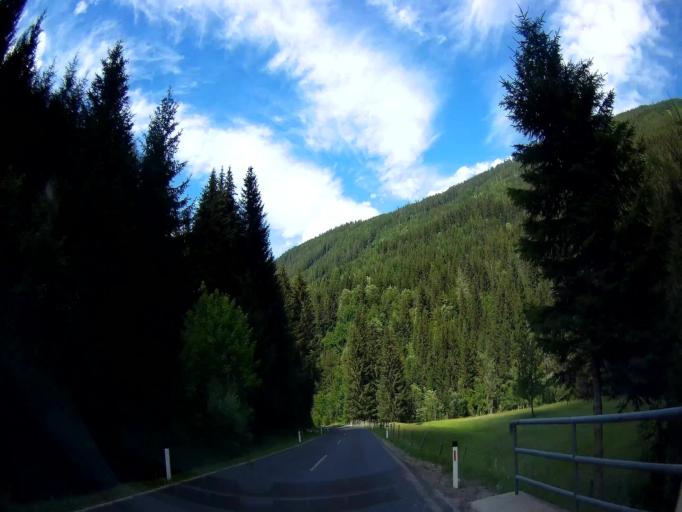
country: AT
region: Styria
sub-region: Politischer Bezirk Murau
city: Stadl an der Mur
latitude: 47.0466
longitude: 14.0000
